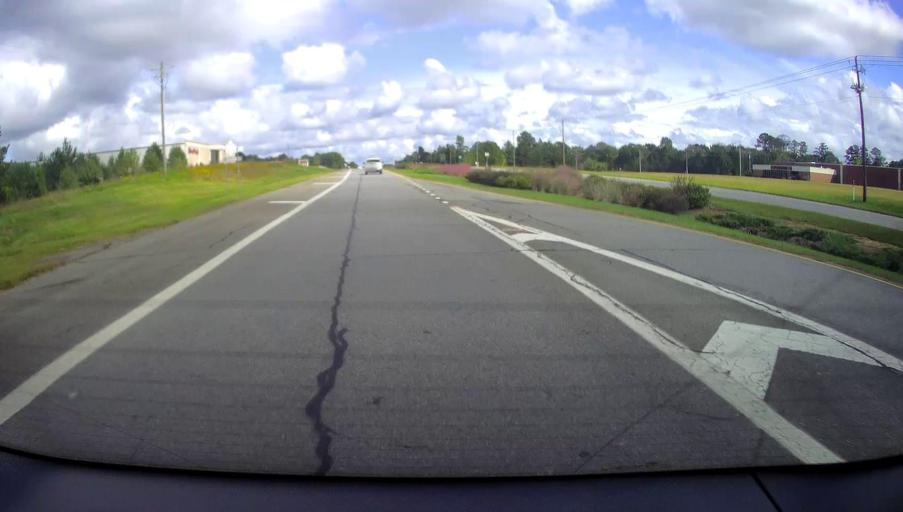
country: US
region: Georgia
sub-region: Baldwin County
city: Milledgeville
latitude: 33.0883
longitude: -83.2865
